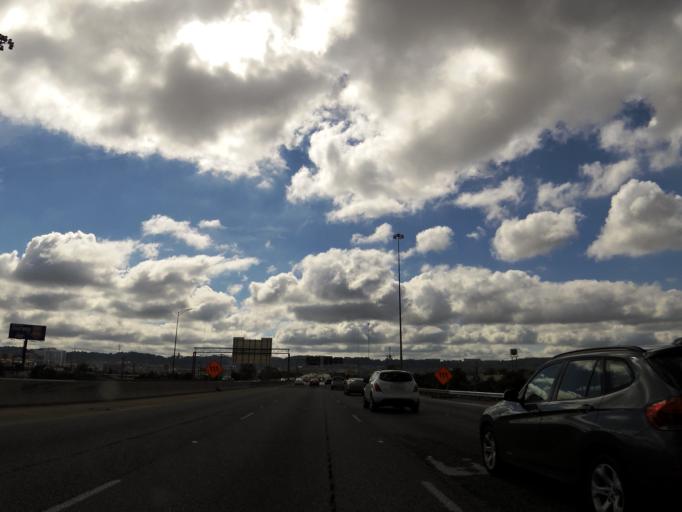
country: US
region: Alabama
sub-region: Jefferson County
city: Birmingham
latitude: 33.5138
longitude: -86.8228
